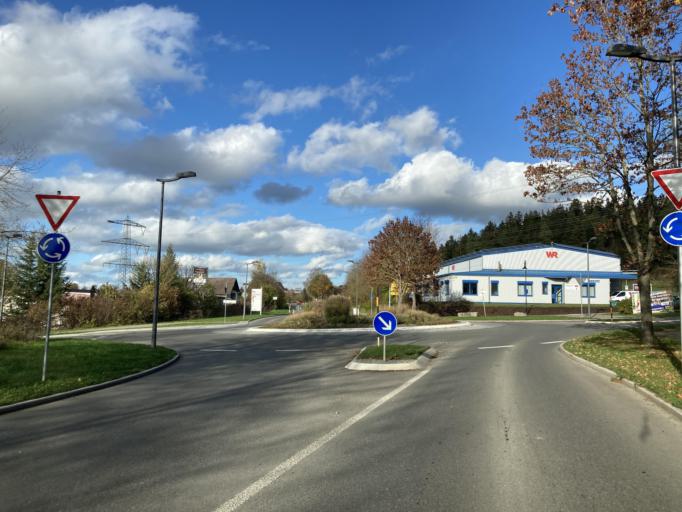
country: DE
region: Baden-Wuerttemberg
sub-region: Freiburg Region
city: Villingen-Schwenningen
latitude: 48.0198
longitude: 8.4710
